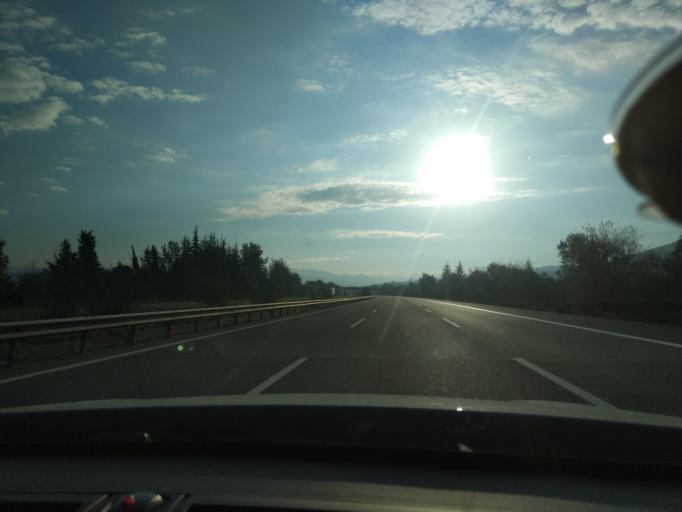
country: TR
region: Duzce
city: Duzce
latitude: 40.7921
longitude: 31.2088
